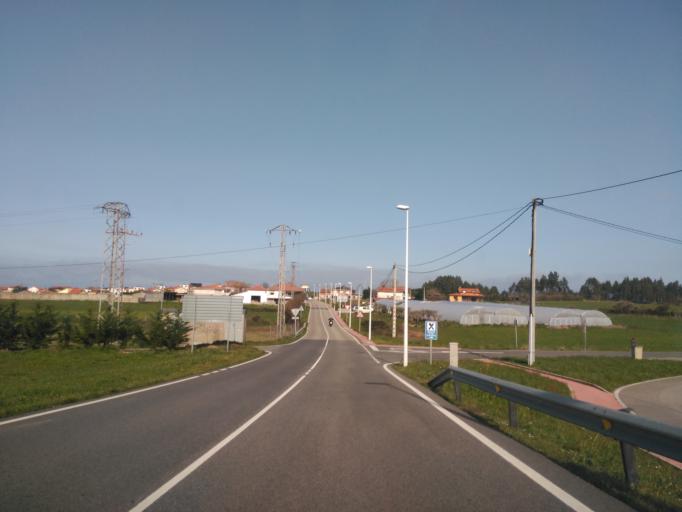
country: ES
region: Cantabria
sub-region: Provincia de Cantabria
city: Suances
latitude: 43.4174
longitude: -4.0687
